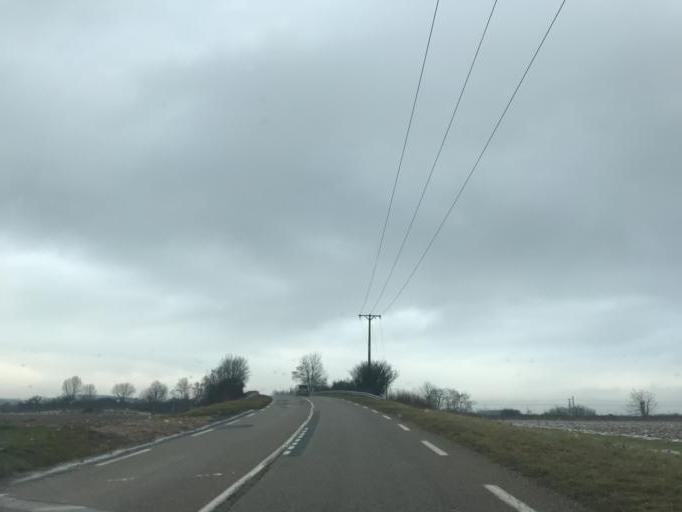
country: FR
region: Rhone-Alpes
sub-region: Departement du Rhone
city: Cailloux-sur-Fontaines
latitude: 45.8580
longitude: 4.8839
